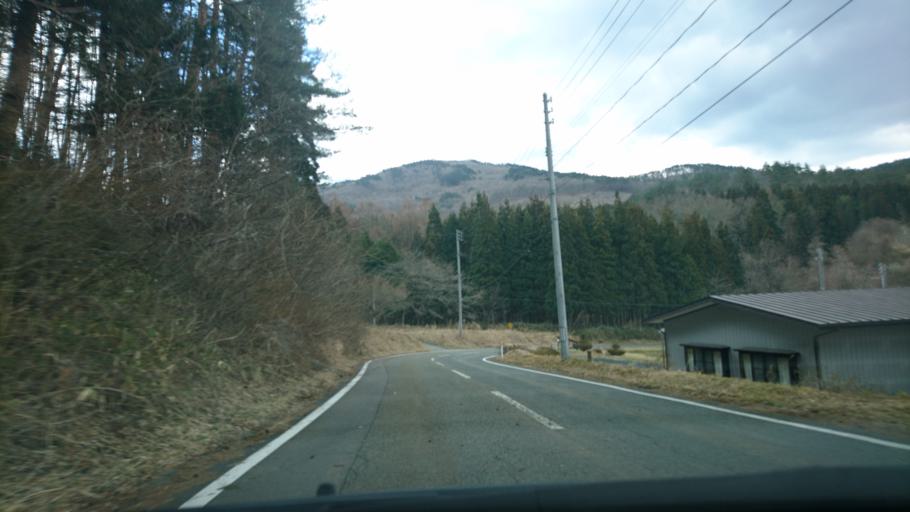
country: JP
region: Iwate
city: Tono
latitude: 39.3440
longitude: 141.3344
